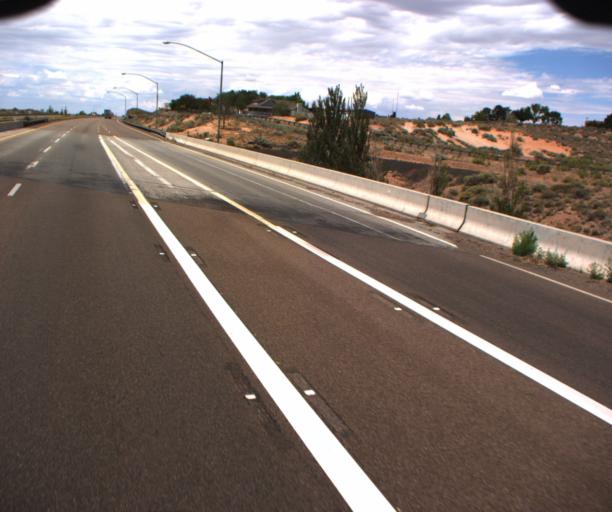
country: US
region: Arizona
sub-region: Navajo County
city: Holbrook
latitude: 34.9129
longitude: -110.1562
